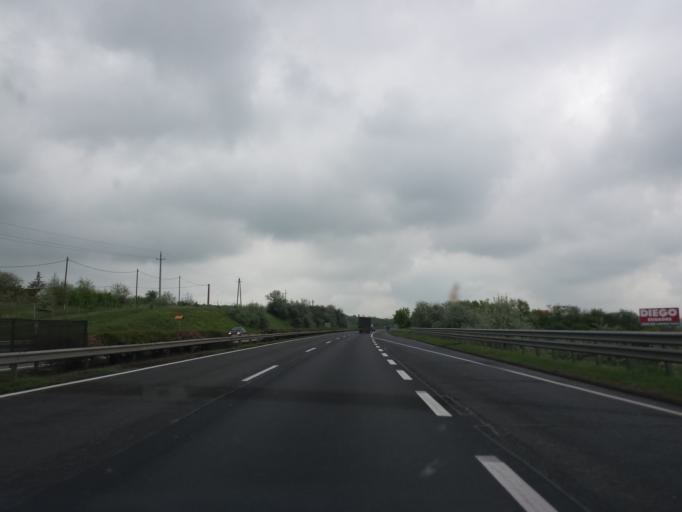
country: HU
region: Pest
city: Biatorbagy
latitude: 47.4920
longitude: 18.8251
